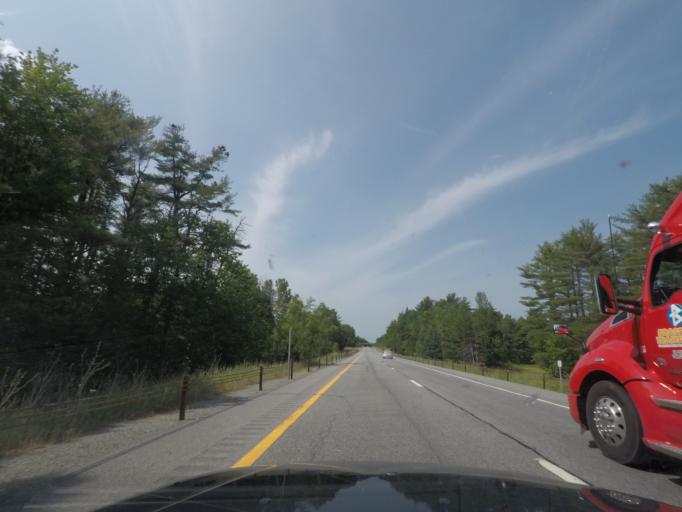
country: US
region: New York
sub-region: Essex County
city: Elizabethtown
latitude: 44.1616
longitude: -73.5833
